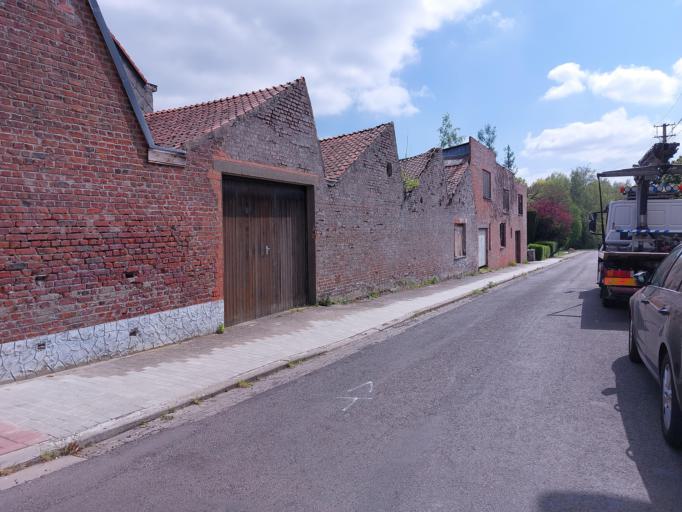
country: BE
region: Wallonia
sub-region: Province du Hainaut
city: Frameries
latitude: 50.4008
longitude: 3.8949
